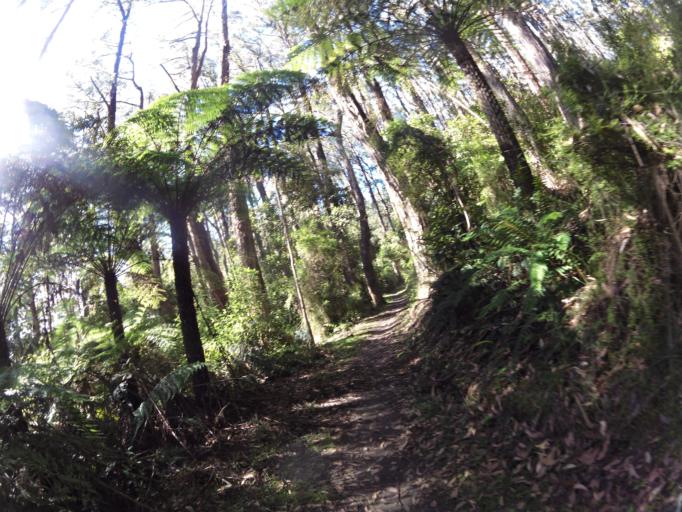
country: AU
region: Victoria
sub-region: Colac-Otway
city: Apollo Bay
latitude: -38.5495
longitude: 143.7397
